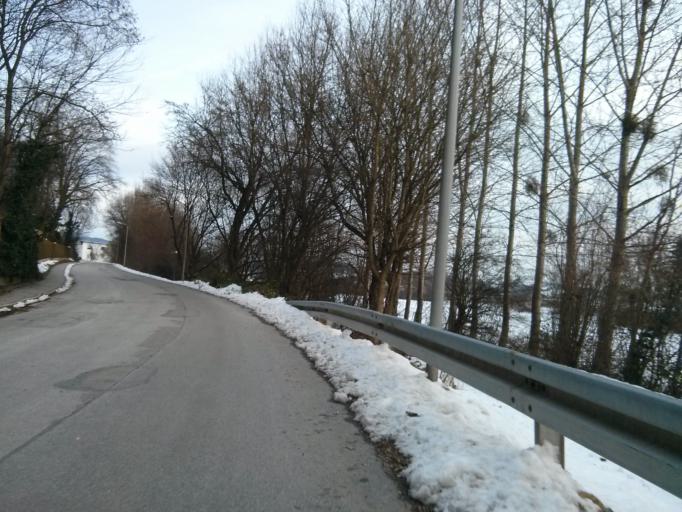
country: DE
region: Bavaria
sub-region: Lower Bavaria
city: Deggendorf
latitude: 48.8361
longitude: 12.9375
